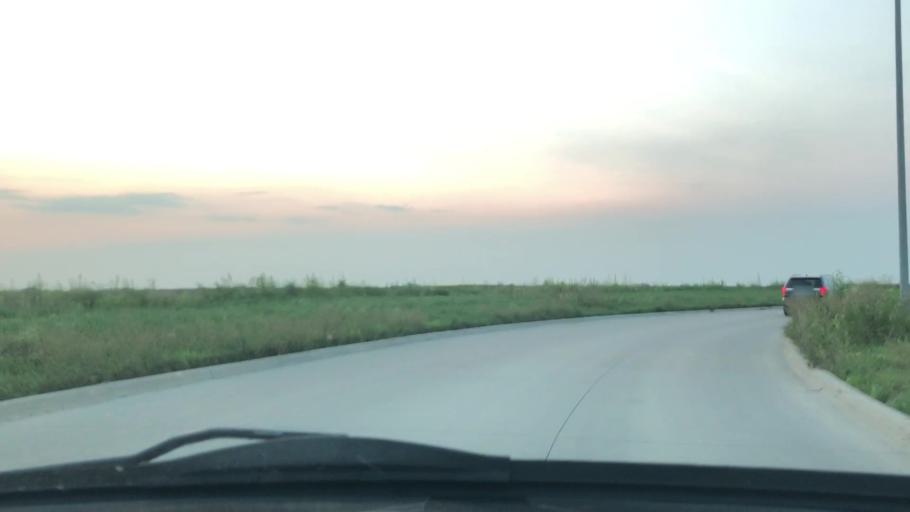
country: US
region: Iowa
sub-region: Johnson County
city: North Liberty
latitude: 41.7168
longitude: -91.6061
